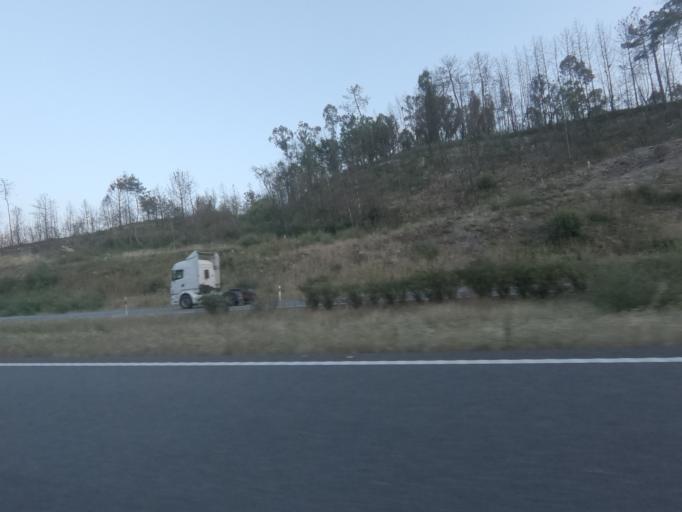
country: ES
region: Galicia
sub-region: Provincia de Pontevedra
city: Ponteareas
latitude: 42.1555
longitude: -8.4929
